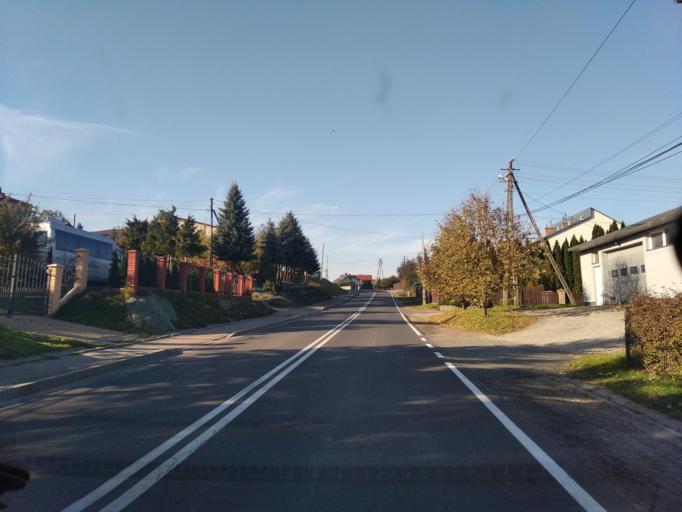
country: PL
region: Subcarpathian Voivodeship
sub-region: Powiat brzozowski
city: Humniska
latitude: 49.6814
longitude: 22.0344
